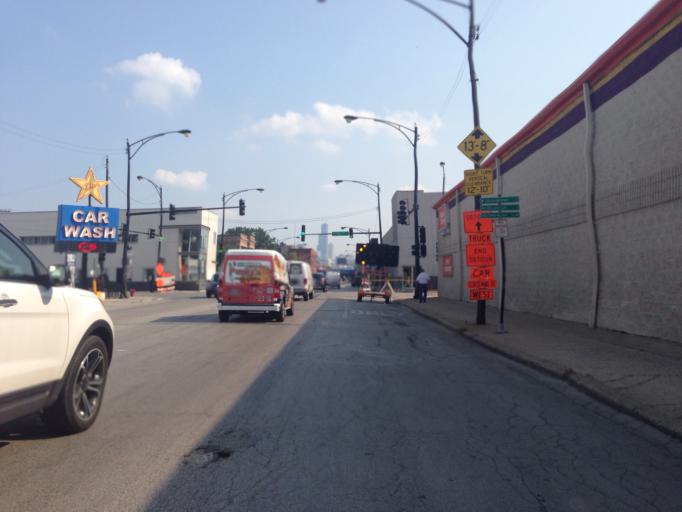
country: US
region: Illinois
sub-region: Cook County
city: Chicago
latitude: 41.9169
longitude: -87.6668
